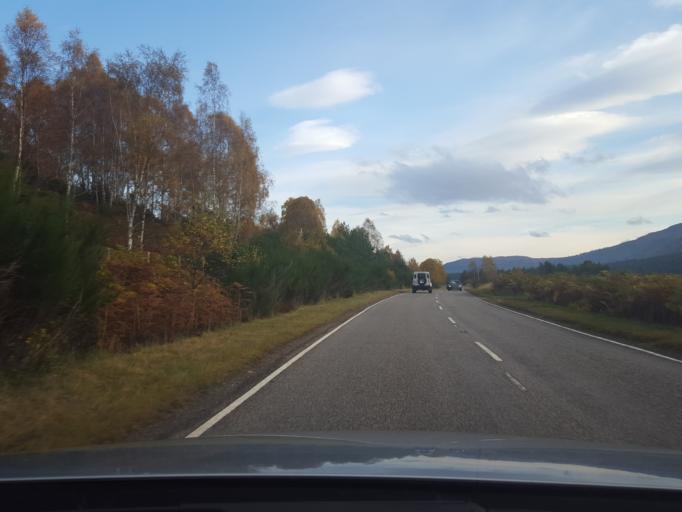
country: GB
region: Scotland
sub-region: Highland
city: Spean Bridge
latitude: 57.1924
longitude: -4.7590
